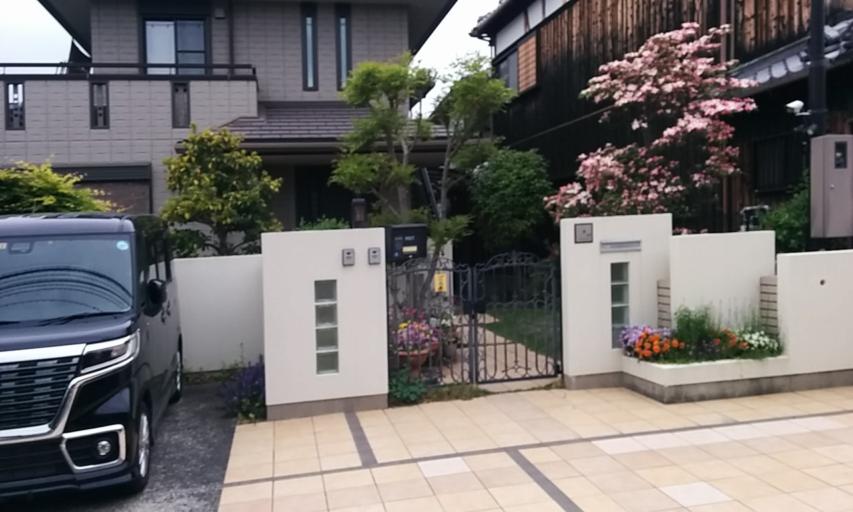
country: JP
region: Shiga Prefecture
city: Kusatsu
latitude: 35.0102
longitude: 135.9555
